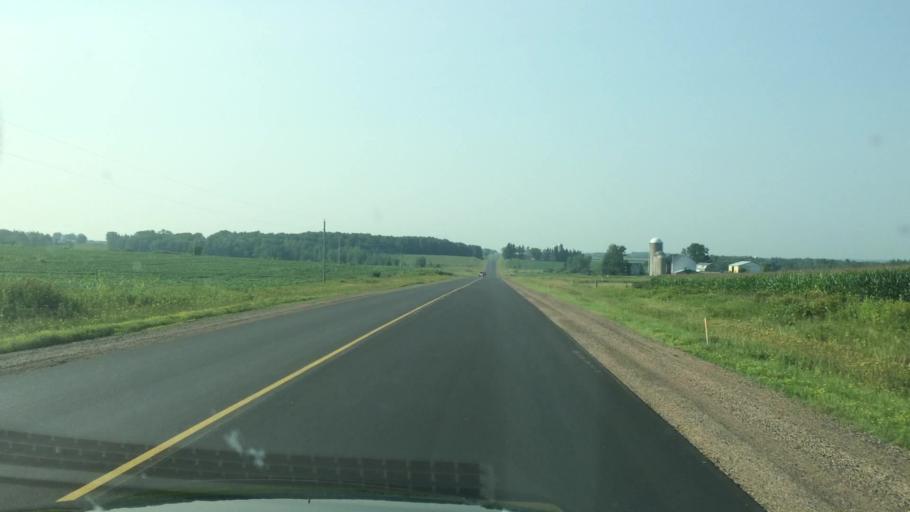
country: US
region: Wisconsin
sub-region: Marathon County
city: Athens
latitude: 44.9194
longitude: -90.0787
